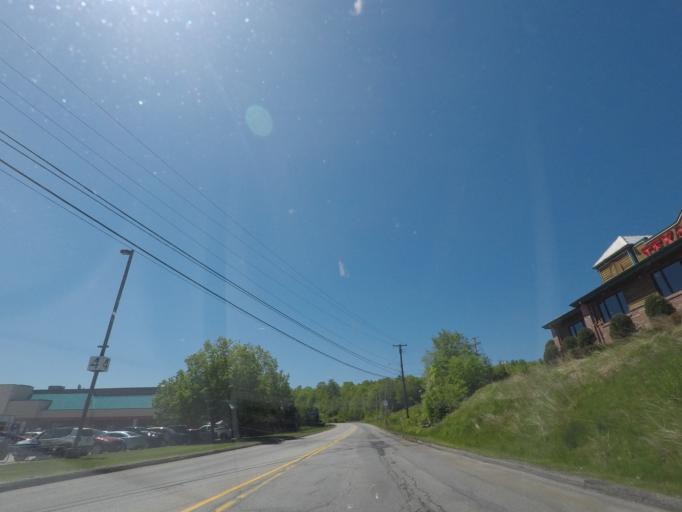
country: US
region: Maine
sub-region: Kennebec County
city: Augusta
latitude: 44.3143
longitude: -69.8129
